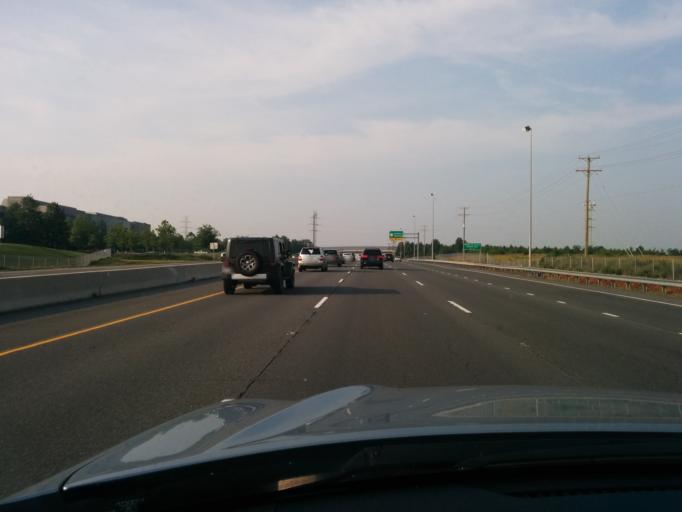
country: US
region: Virginia
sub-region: Loudoun County
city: Sterling
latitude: 39.0153
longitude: -77.4327
